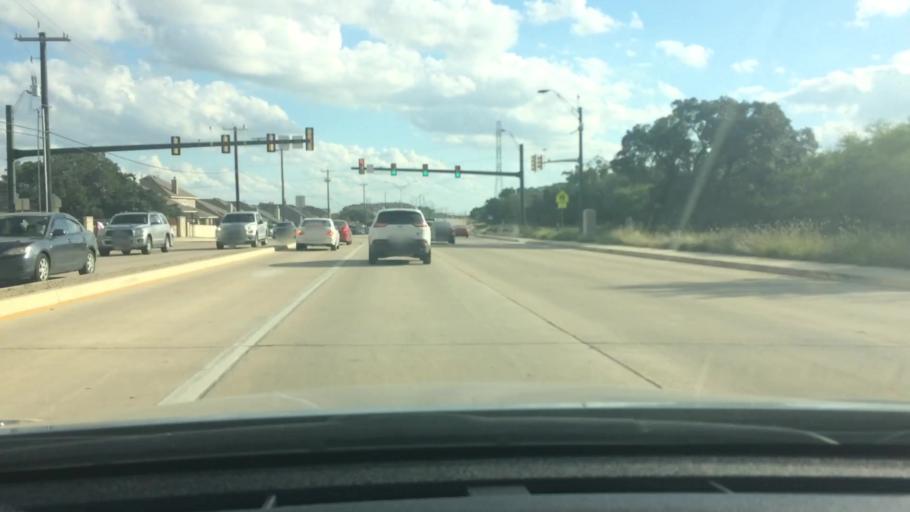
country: US
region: Texas
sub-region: Bexar County
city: Hollywood Park
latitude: 29.6389
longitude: -98.4246
